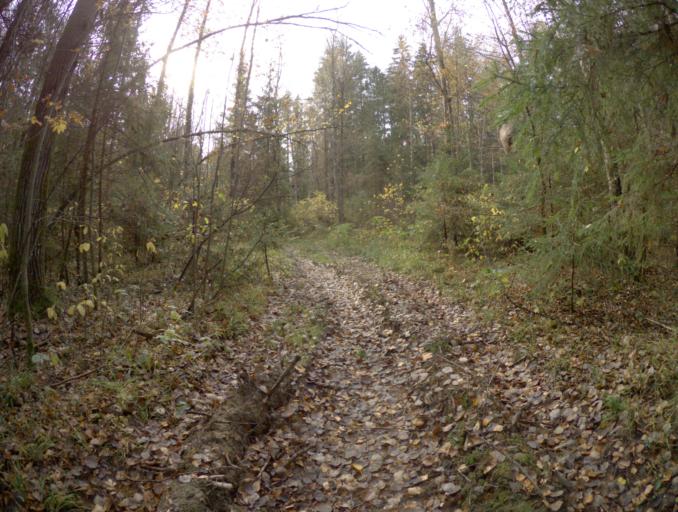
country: RU
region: Vladimir
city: Raduzhnyy
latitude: 55.9597
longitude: 40.3534
